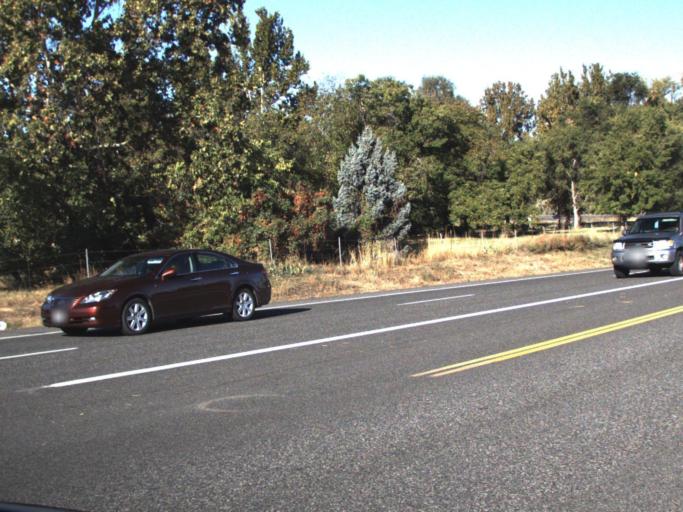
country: US
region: Washington
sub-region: Benton County
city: West Richland
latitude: 46.2968
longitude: -119.3253
